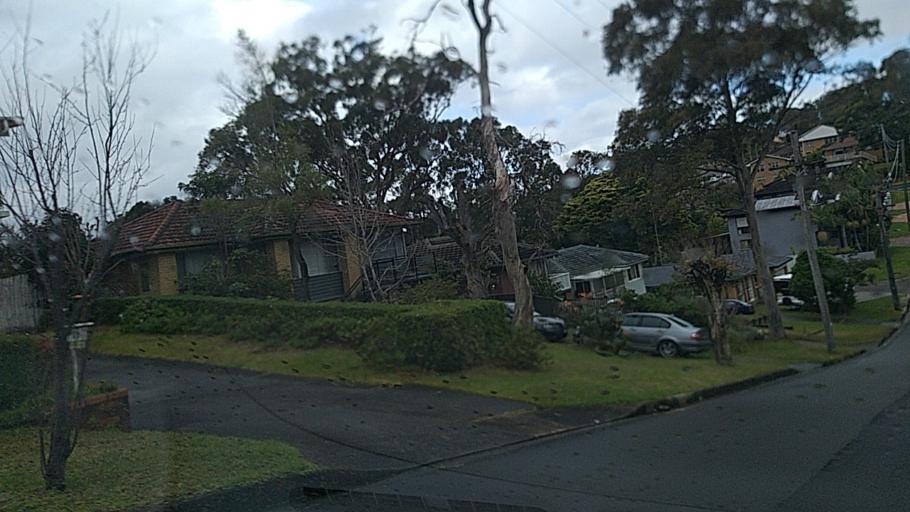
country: AU
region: New South Wales
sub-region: Wollongong
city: Mount Keira
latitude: -34.4248
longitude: 150.8552
